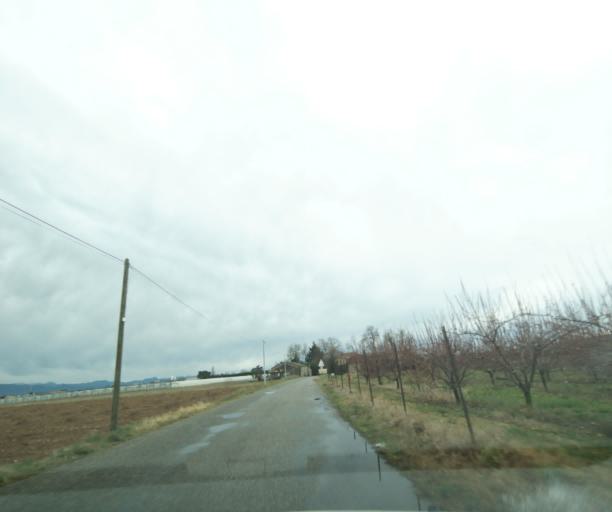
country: FR
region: Rhone-Alpes
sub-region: Departement de la Drome
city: Bourg-les-Valence
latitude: 44.9614
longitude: 4.9149
